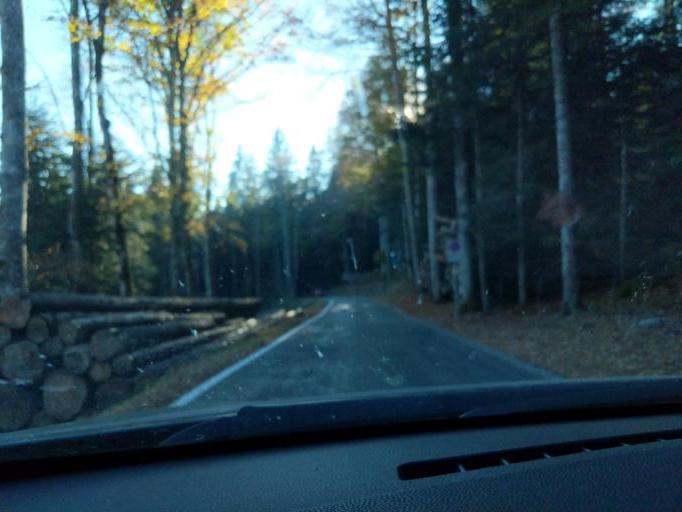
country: CH
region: Neuchatel
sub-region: Neuchatel District
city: Le Landeron
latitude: 47.1137
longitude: 7.0484
